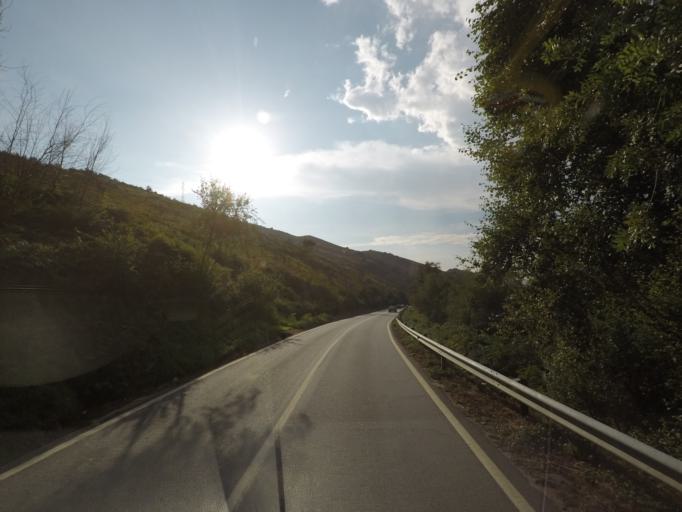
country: PT
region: Porto
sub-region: Baiao
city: Valadares
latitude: 41.1974
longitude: -7.9492
